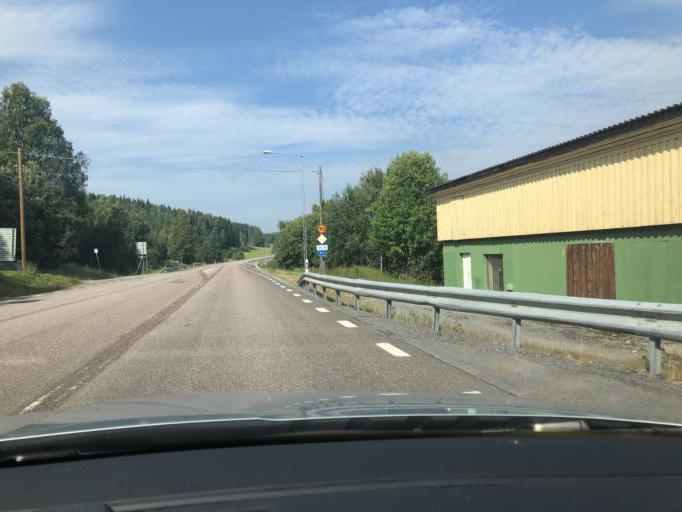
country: SE
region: Vaesternorrland
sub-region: Kramfors Kommun
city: Kramfors
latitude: 62.8187
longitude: 17.8554
